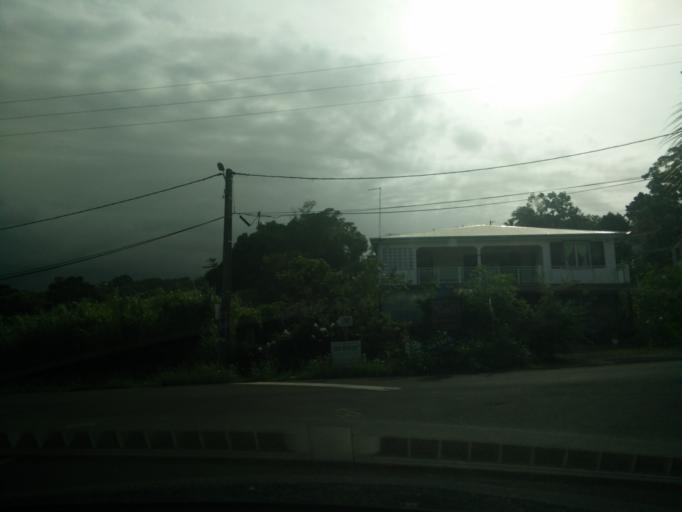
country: GP
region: Guadeloupe
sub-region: Guadeloupe
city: Petit-Bourg
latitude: 16.1271
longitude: -61.5934
